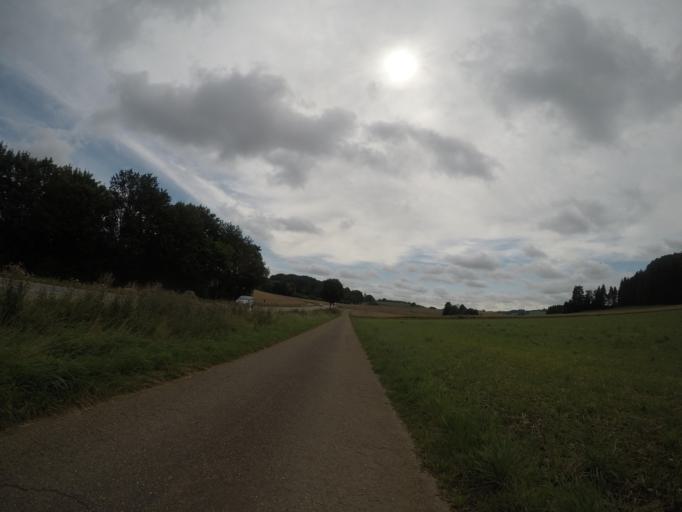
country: DE
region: Baden-Wuerttemberg
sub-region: Tuebingen Region
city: Laichingen
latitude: 48.4704
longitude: 9.6446
